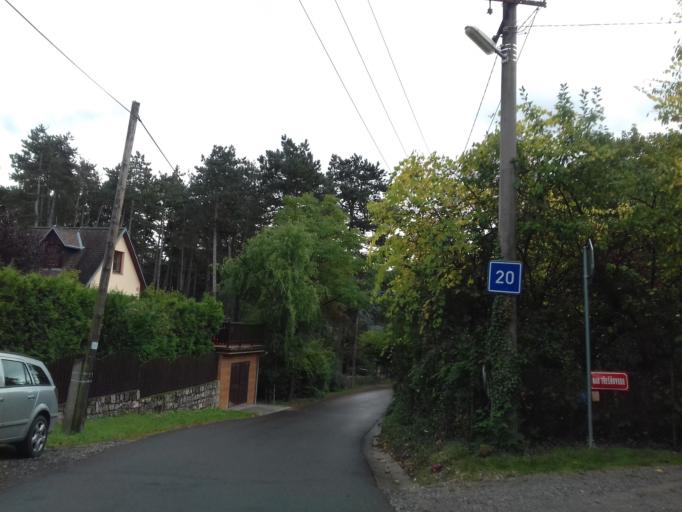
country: CZ
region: Central Bohemia
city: Revnice
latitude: 49.9227
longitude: 14.2382
